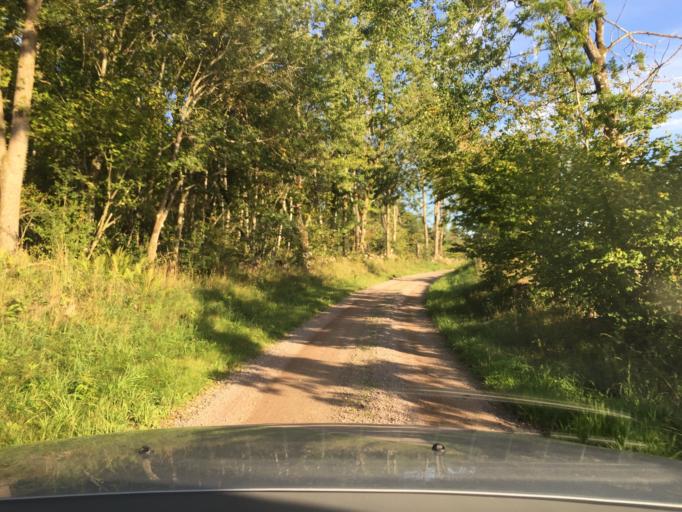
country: SE
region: Skane
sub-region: Hassleholms Kommun
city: Sosdala
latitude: 56.0212
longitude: 13.7073
